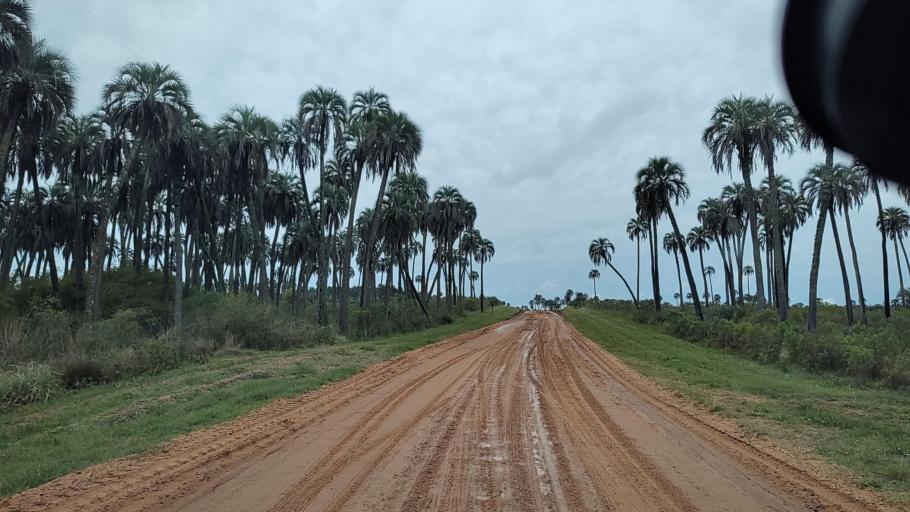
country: AR
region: Entre Rios
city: Ubajay
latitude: -31.8516
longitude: -58.3140
